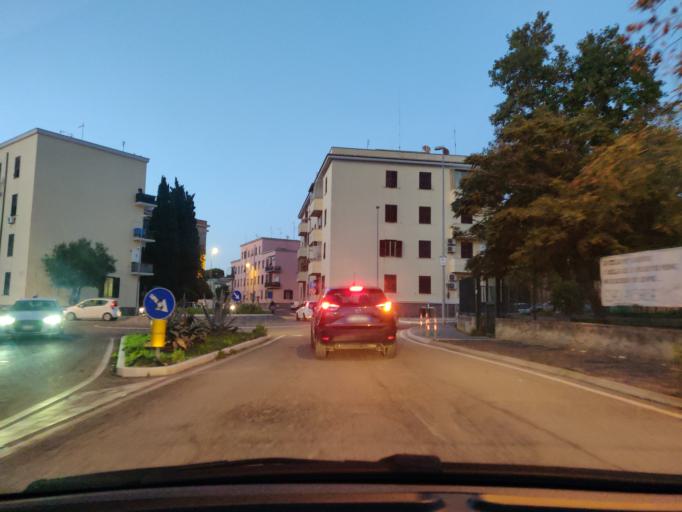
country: IT
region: Latium
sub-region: Citta metropolitana di Roma Capitale
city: Civitavecchia
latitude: 42.0880
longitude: 11.8076
